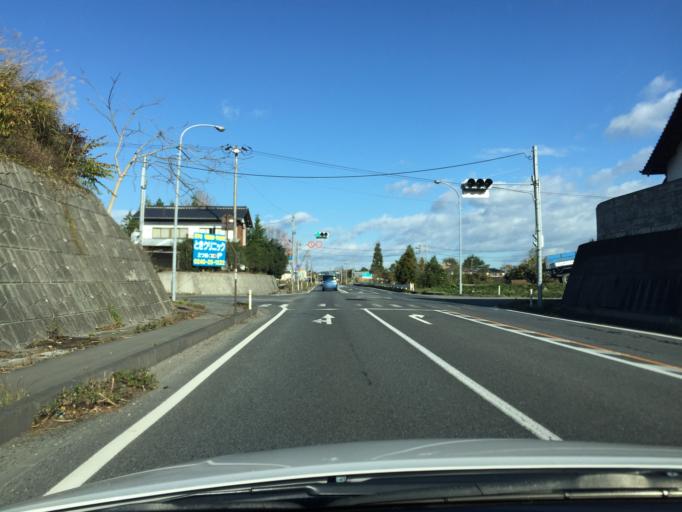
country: JP
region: Fukushima
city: Namie
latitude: 37.2558
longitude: 140.9981
